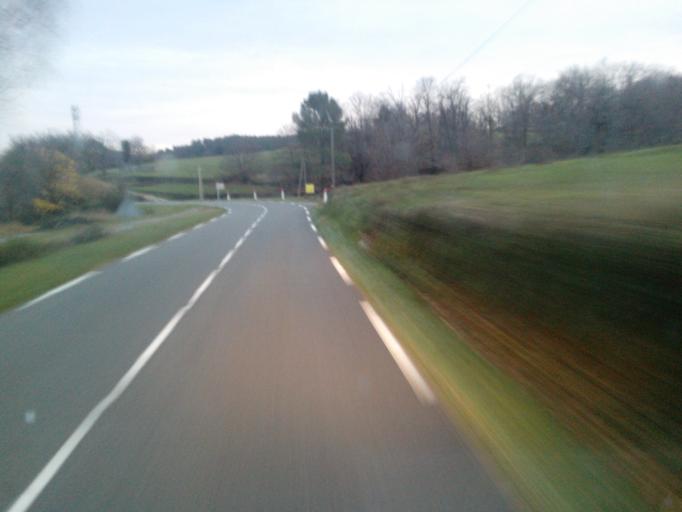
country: FR
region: Languedoc-Roussillon
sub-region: Departement du Gard
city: Saint-Jean-du-Gard
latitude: 44.1502
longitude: 3.7665
